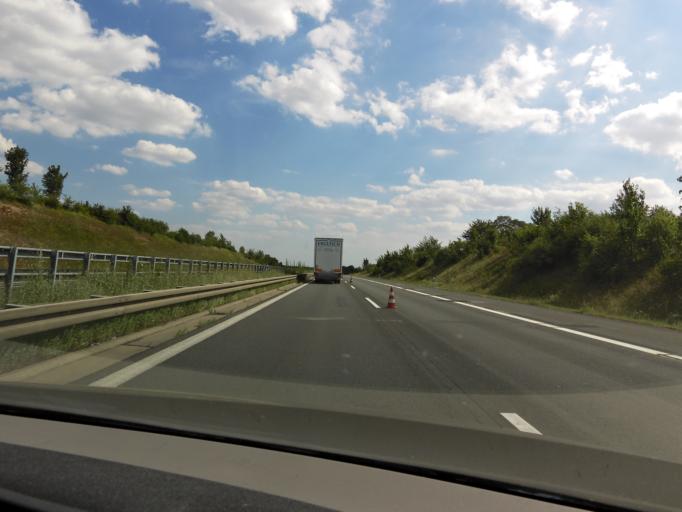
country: DE
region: Saxony-Anhalt
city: Beesenlaublingen
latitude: 51.7013
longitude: 11.7268
